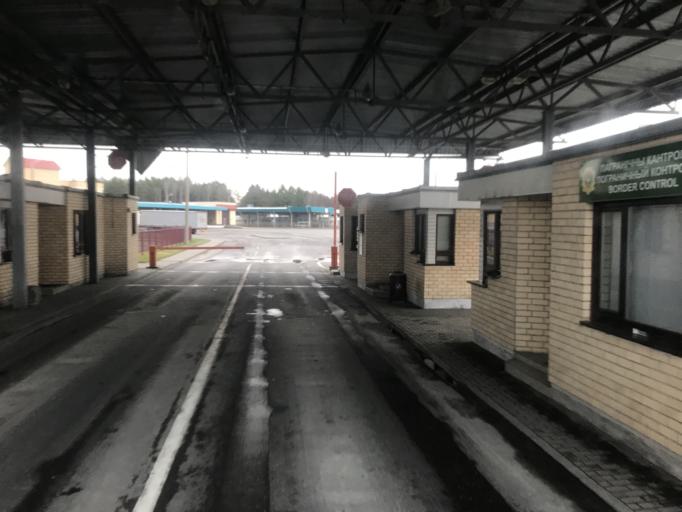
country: BY
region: Grodnenskaya
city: Vyalikaya Byerastavitsa
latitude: 53.1228
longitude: 23.8964
